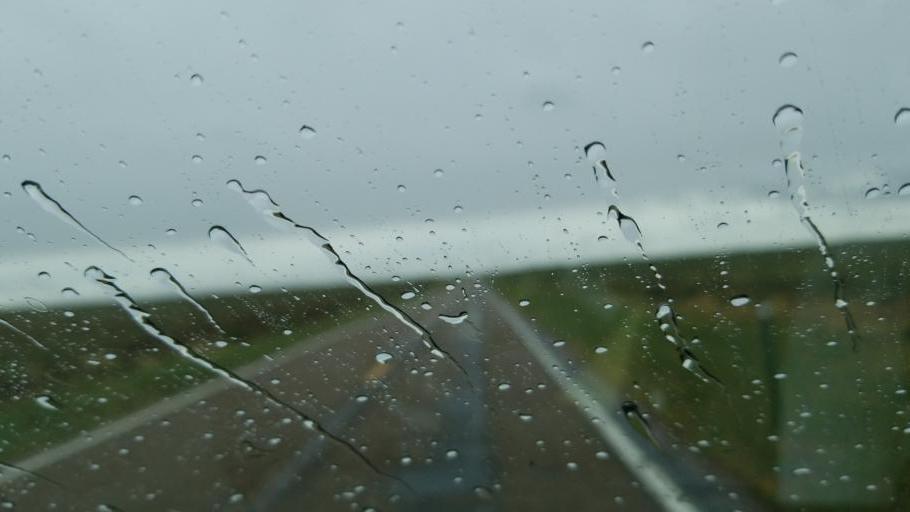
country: US
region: Colorado
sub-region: Lincoln County
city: Hugo
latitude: 38.8495
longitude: -103.2240
